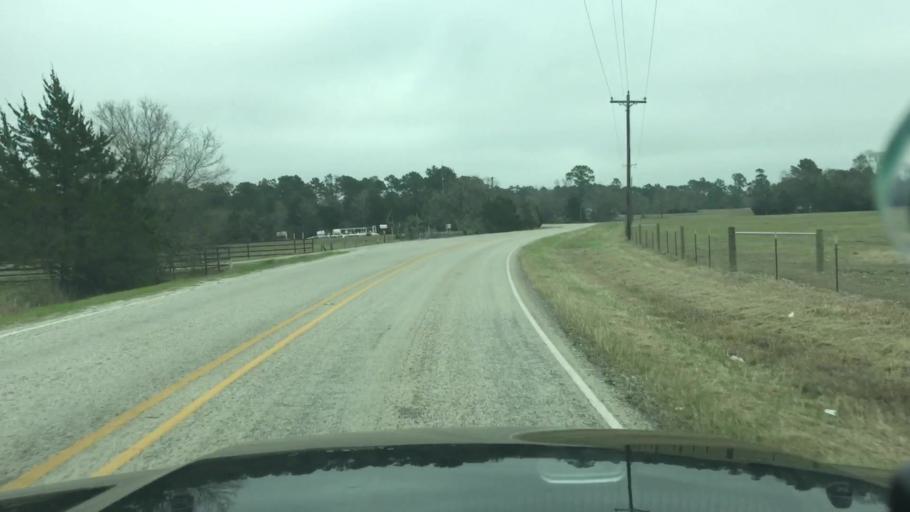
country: US
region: Texas
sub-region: Fayette County
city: La Grange
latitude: 30.0129
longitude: -96.9307
